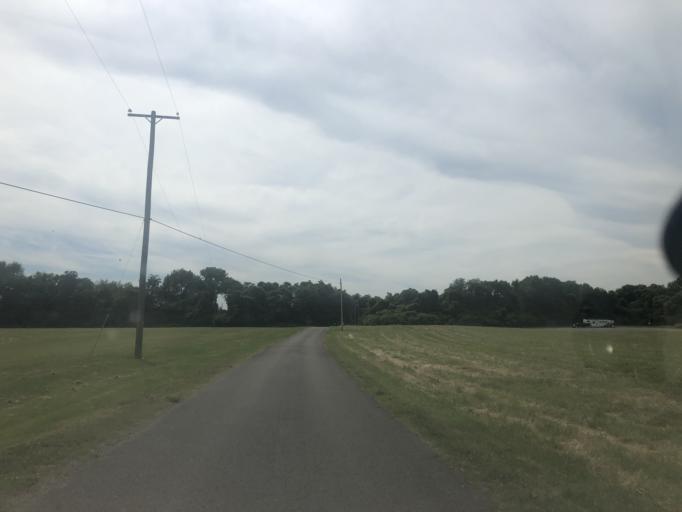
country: US
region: Tennessee
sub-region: Davidson County
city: Lakewood
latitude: 36.2028
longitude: -86.6572
